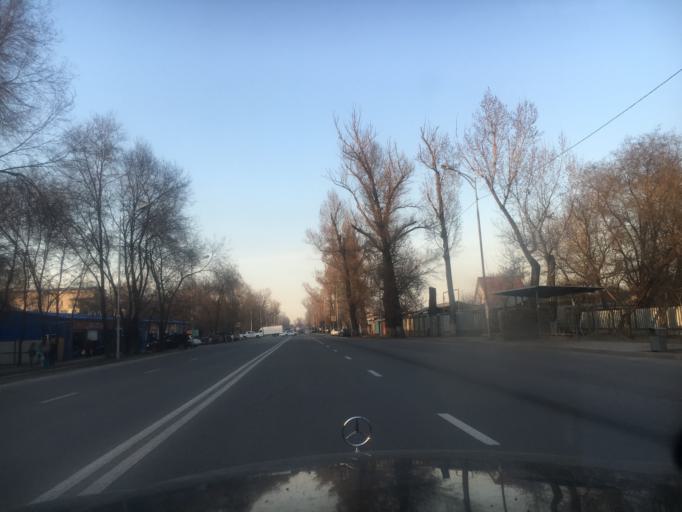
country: KZ
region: Almaty Oblysy
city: Pervomayskiy
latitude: 43.3745
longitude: 76.9916
